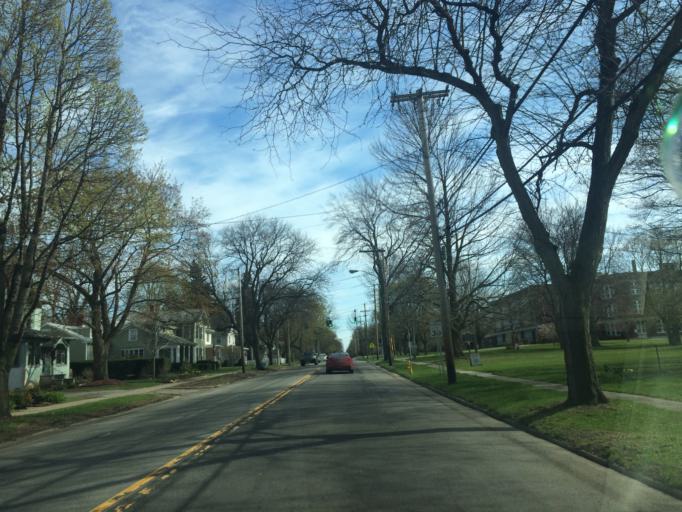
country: US
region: New York
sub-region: Monroe County
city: Webster
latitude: 43.2098
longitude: -77.4304
